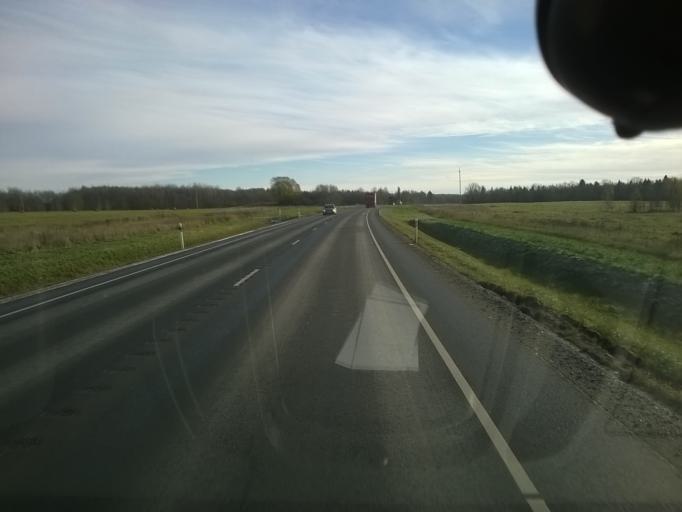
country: EE
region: Harju
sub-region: Saue vald
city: Laagri
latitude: 59.3309
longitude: 24.6280
